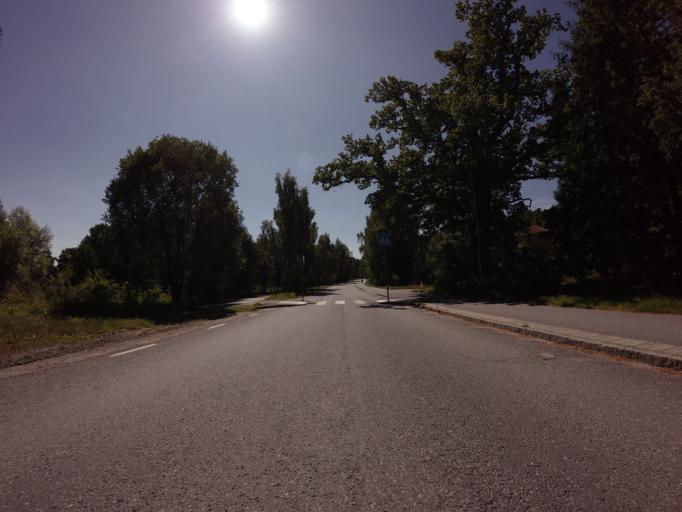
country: SE
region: Stockholm
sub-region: Lidingo
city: Brevik
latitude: 59.3584
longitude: 18.2233
